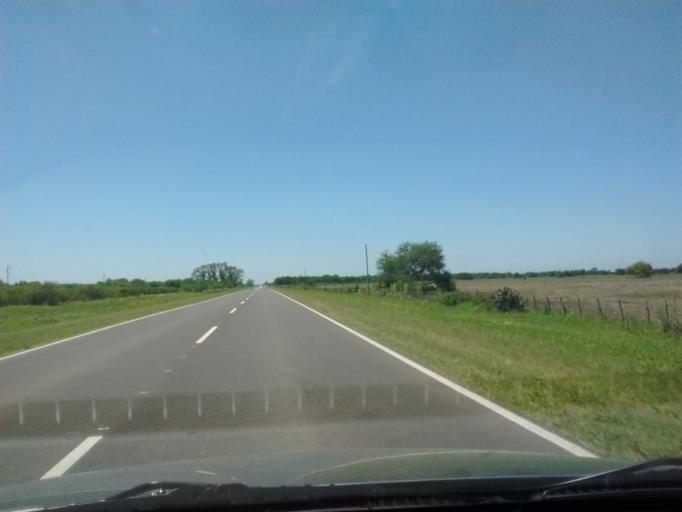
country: AR
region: Entre Rios
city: General Galarza
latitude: -32.8670
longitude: -59.7287
